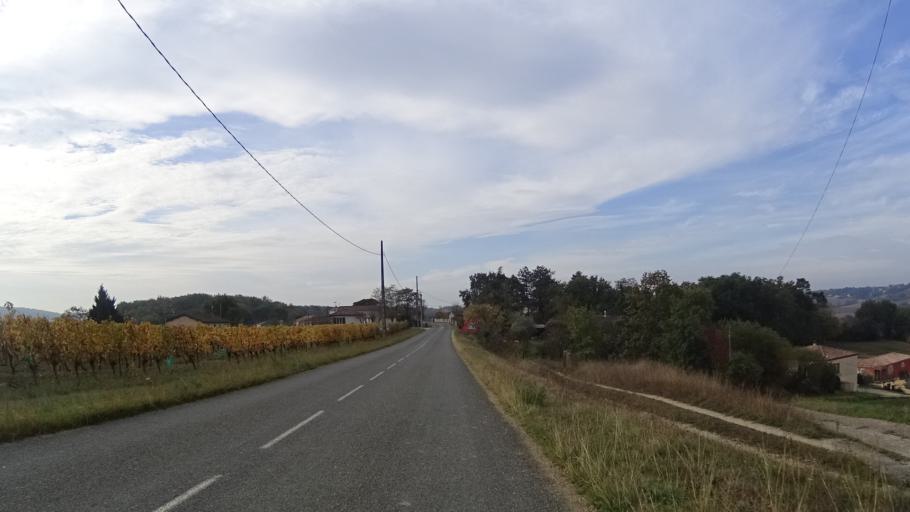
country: FR
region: Aquitaine
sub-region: Departement du Lot-et-Garonne
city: Boe
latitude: 44.1327
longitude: 0.6004
